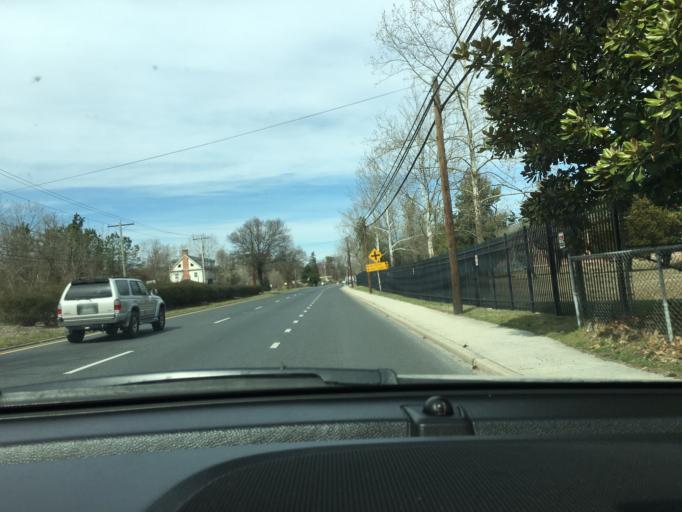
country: US
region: Maryland
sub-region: Wicomico County
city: Salisbury
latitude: 38.3744
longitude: -75.6168
